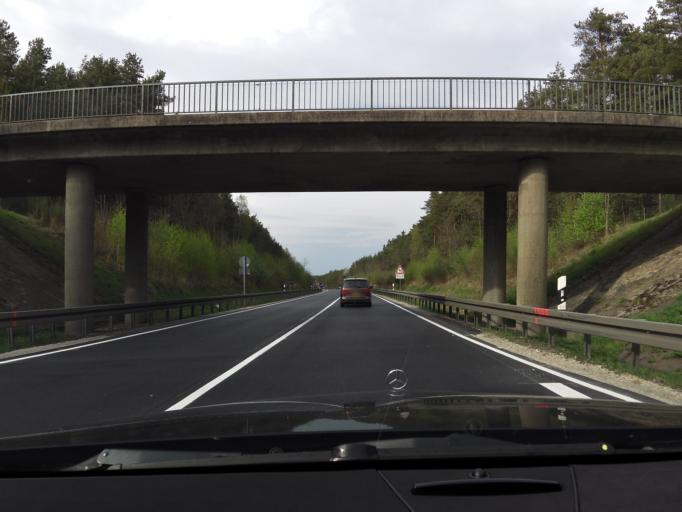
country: DE
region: Bavaria
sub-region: Regierungsbezirk Mittelfranken
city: Hochstadt an der Aisch
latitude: 49.7313
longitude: 10.8252
